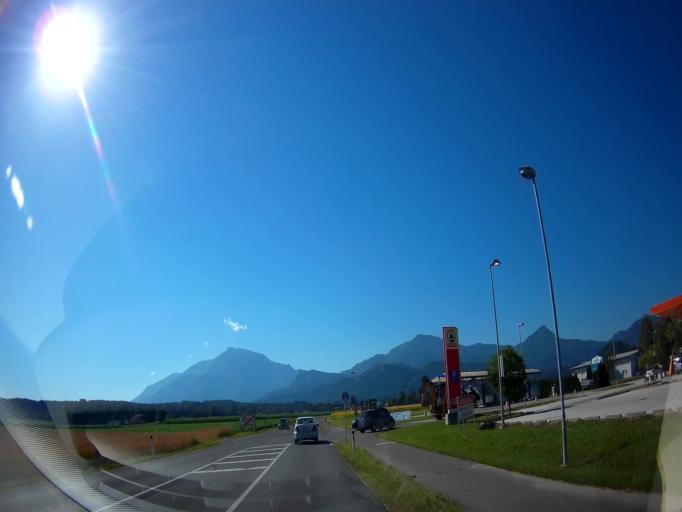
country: AT
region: Carinthia
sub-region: Politischer Bezirk Volkermarkt
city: Eberndorf
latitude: 46.5852
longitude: 14.6501
